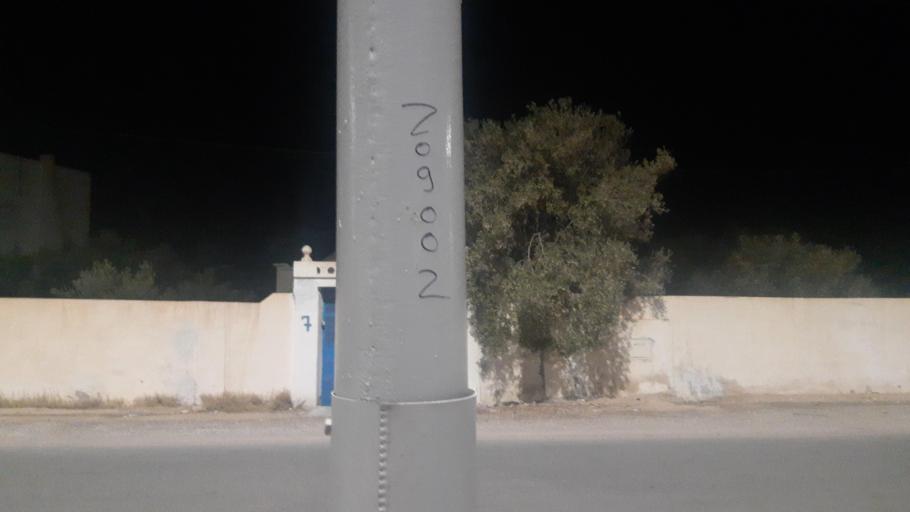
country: TN
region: Madanin
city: Midoun
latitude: 33.8207
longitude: 11.0399
